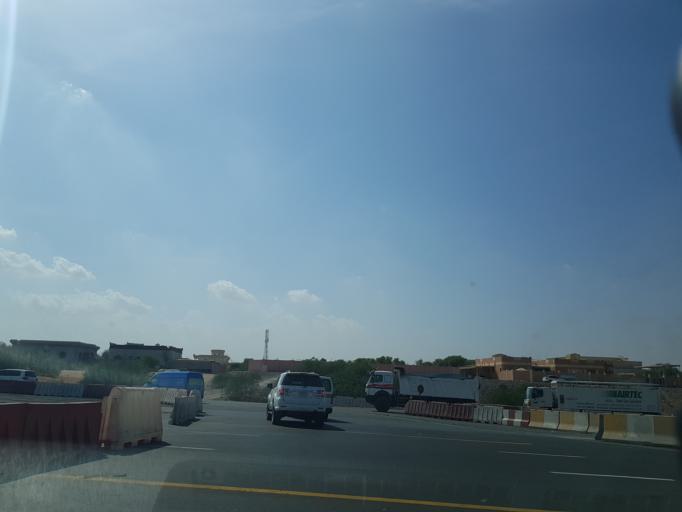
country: AE
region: Ra's al Khaymah
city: Ras al-Khaimah
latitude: 25.7016
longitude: 55.9626
